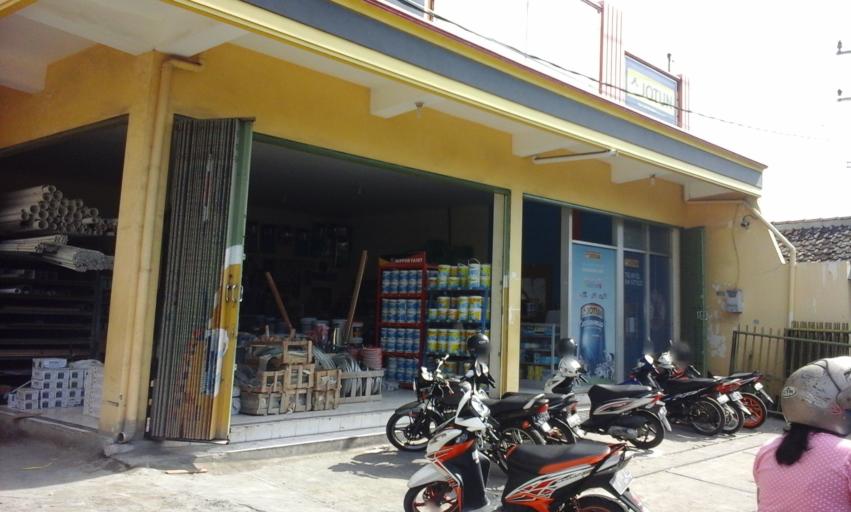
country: ID
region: East Java
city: Krajan
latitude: -8.2143
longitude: 114.3444
